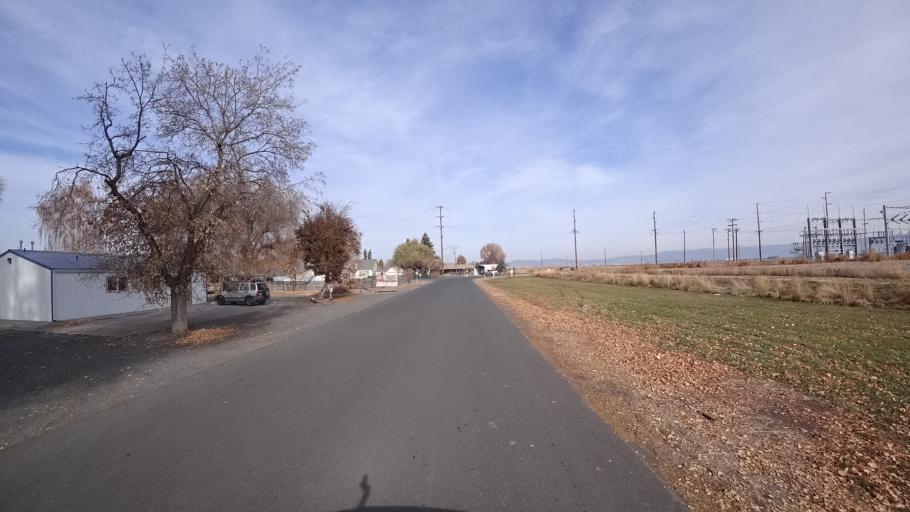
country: US
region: California
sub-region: Siskiyou County
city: Tulelake
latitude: 41.9528
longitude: -121.4724
